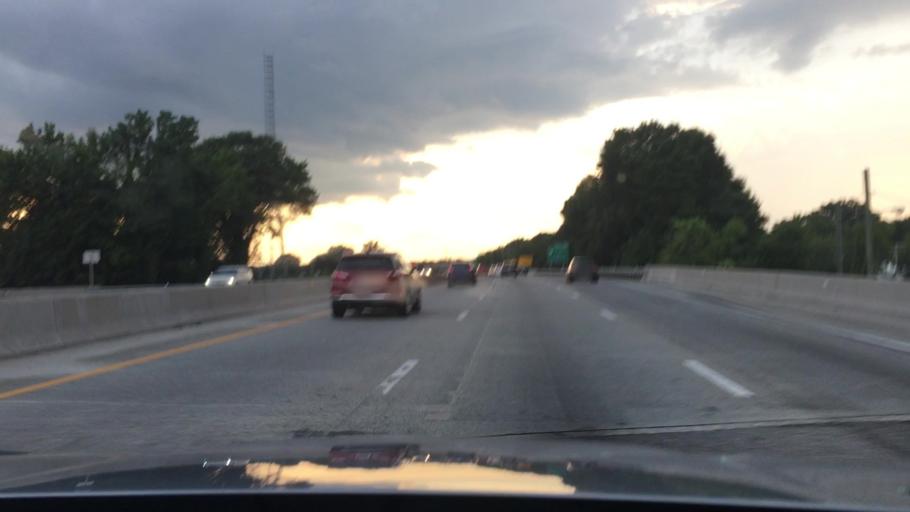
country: US
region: Virginia
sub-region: City of Richmond
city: Richmond
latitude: 37.5759
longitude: -77.4627
